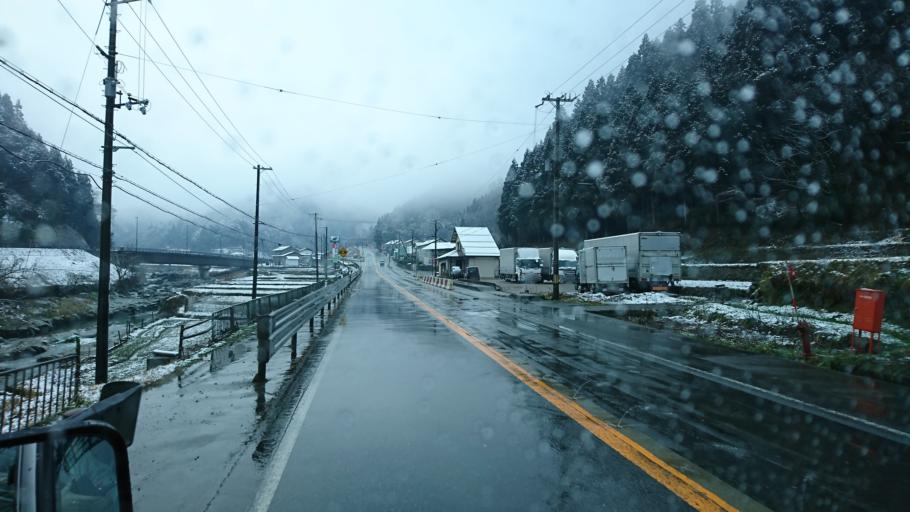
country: JP
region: Hyogo
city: Toyooka
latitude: 35.4908
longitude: 134.5583
